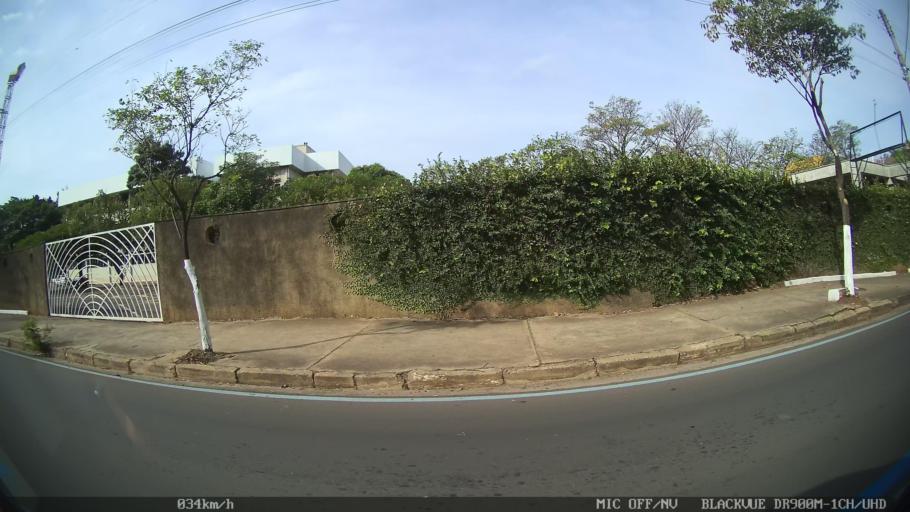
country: BR
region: Sao Paulo
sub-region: Piracicaba
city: Piracicaba
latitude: -22.7299
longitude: -47.6270
